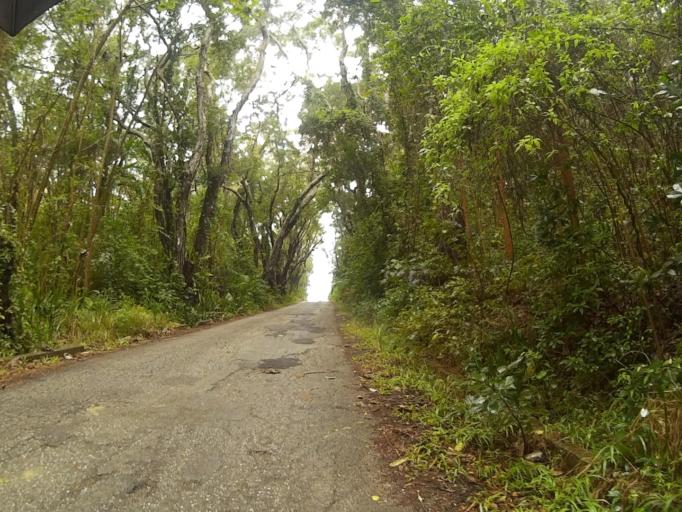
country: BB
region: Saint Andrew
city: Greenland
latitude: 13.2745
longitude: -59.5861
